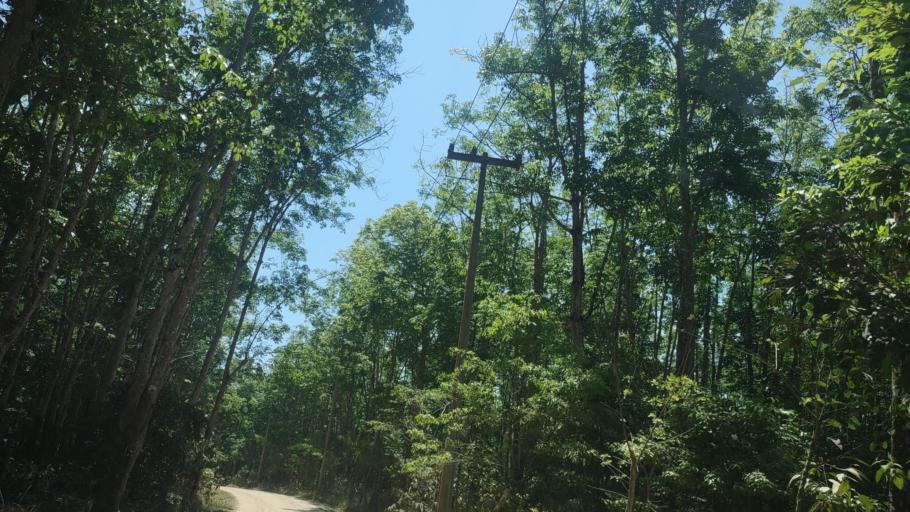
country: MX
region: Veracruz
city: Las Choapas
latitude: 17.7738
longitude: -94.1480
